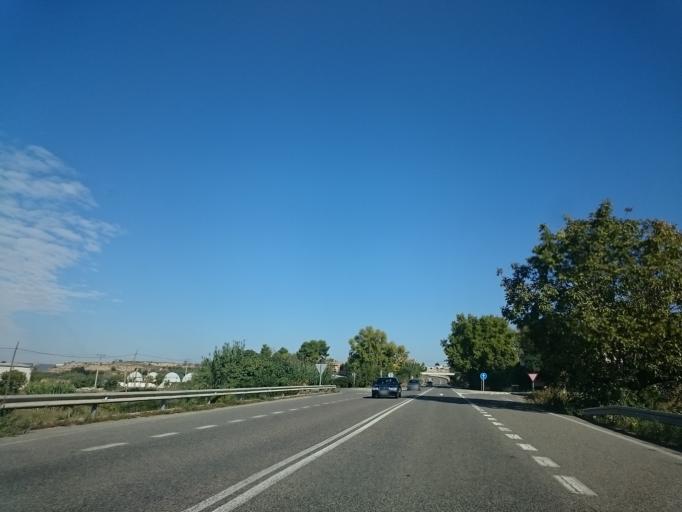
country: ES
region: Catalonia
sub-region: Provincia de Lleida
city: Juneda
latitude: 41.5455
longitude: 0.8215
